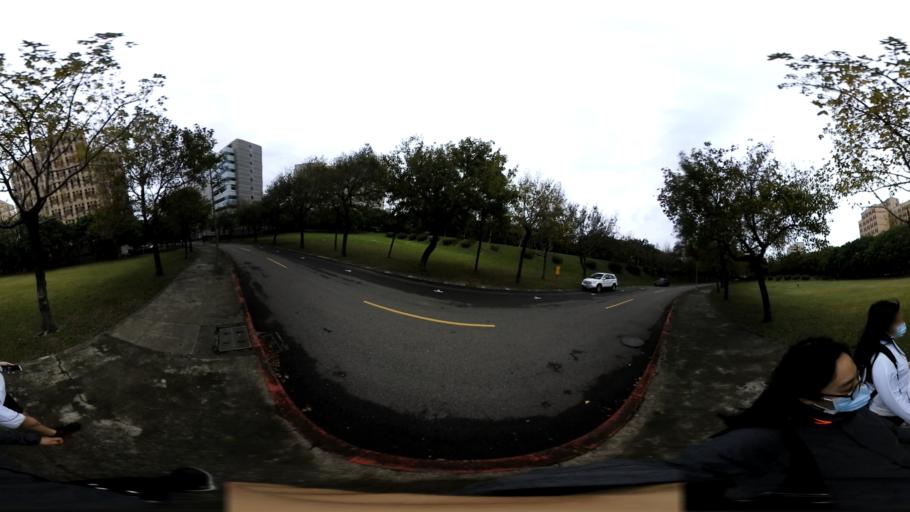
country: TW
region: Taiwan
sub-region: Hsinchu
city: Hsinchu
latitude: 24.7840
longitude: 120.9998
